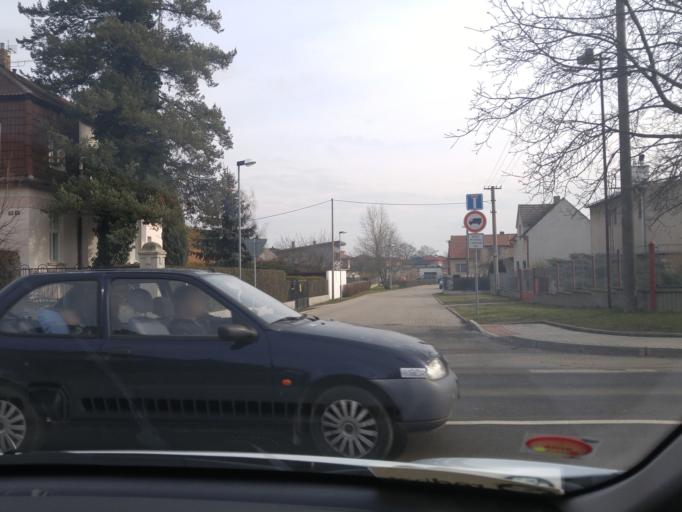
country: CZ
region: Central Bohemia
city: Kostelec nad Labem
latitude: 50.2223
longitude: 14.5826
